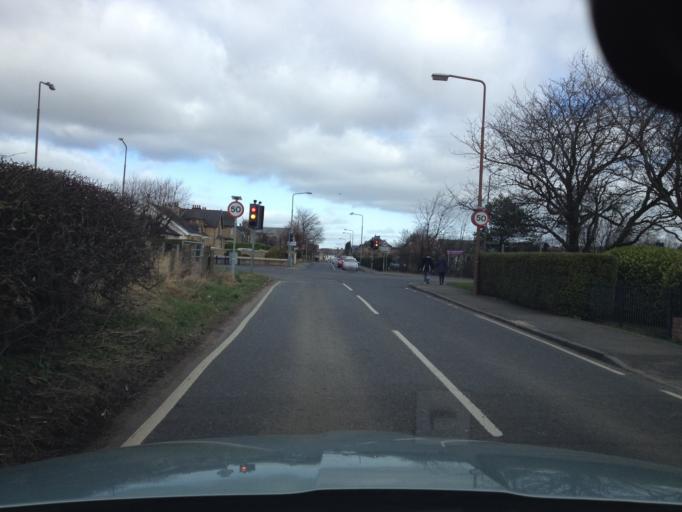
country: GB
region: Scotland
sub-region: West Lothian
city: Broxburn
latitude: 55.9301
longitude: -3.4698
